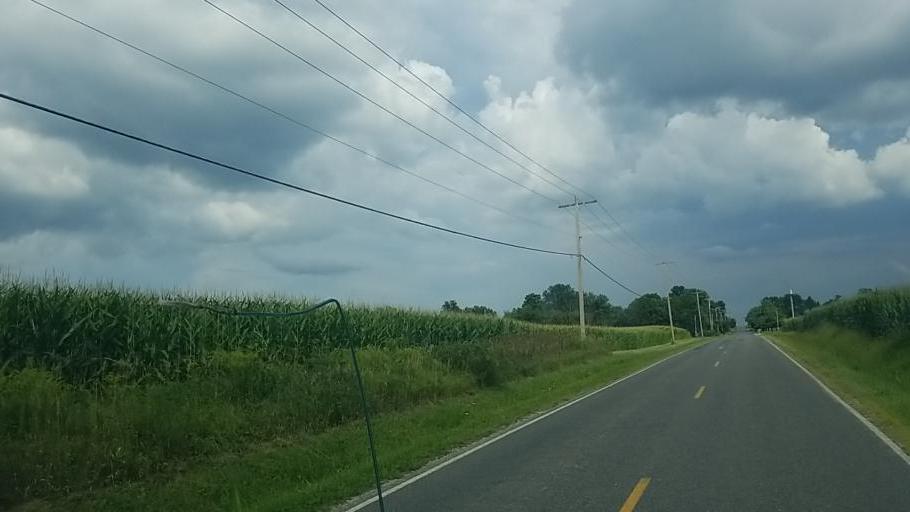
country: US
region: Ohio
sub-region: Medina County
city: Westfield Center
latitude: 41.0120
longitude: -81.9185
